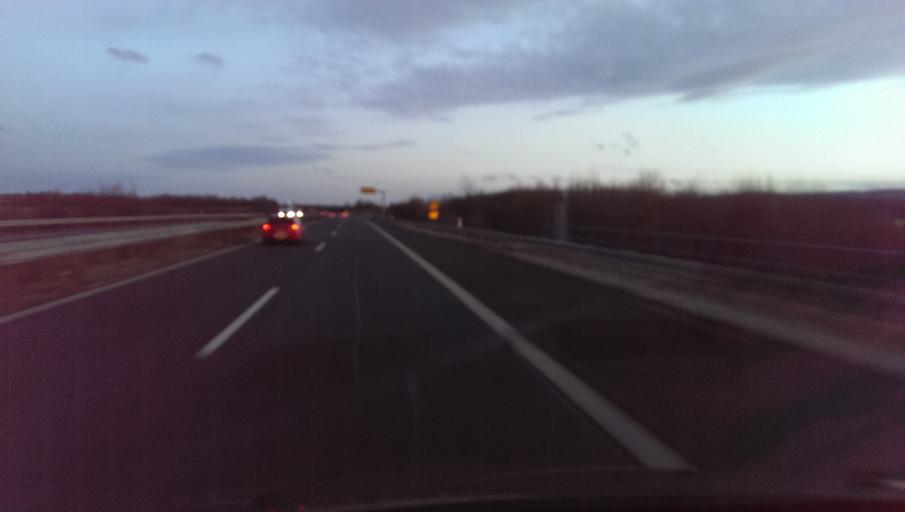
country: DE
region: Saxony-Anhalt
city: Stapelburg
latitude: 51.9081
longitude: 10.6747
